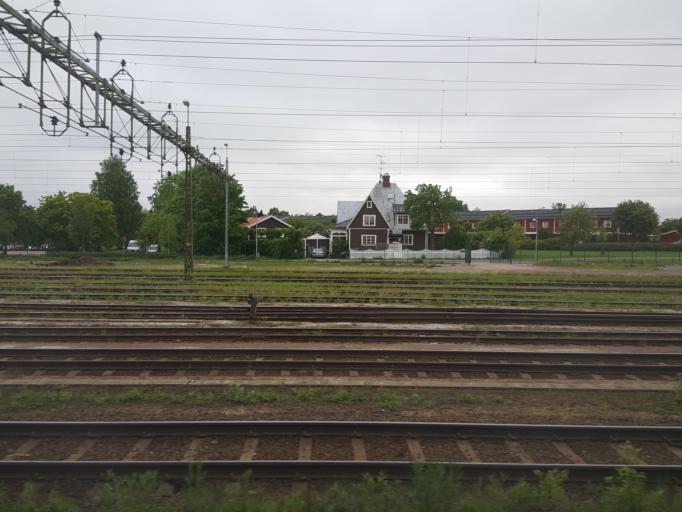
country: SE
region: Dalarna
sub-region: Avesta Kommun
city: Avesta
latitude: 60.1316
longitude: 16.2151
